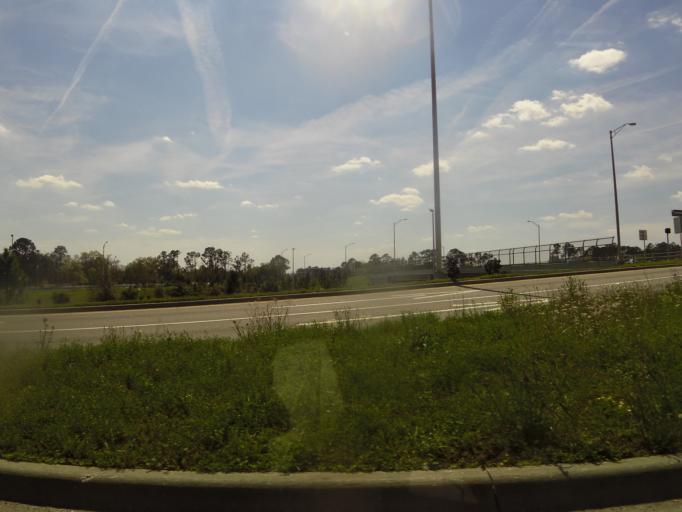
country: US
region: Florida
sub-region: Duval County
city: Jacksonville
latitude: 30.3156
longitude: -81.7921
